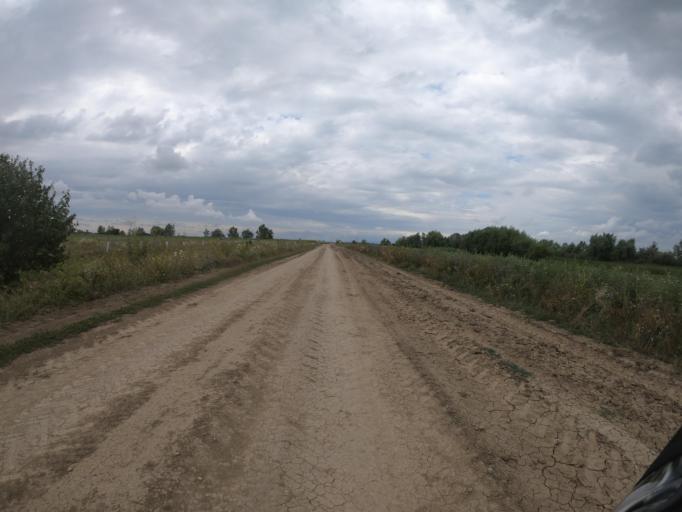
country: HU
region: Jasz-Nagykun-Szolnok
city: Tiszafured
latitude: 47.7207
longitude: 20.7921
